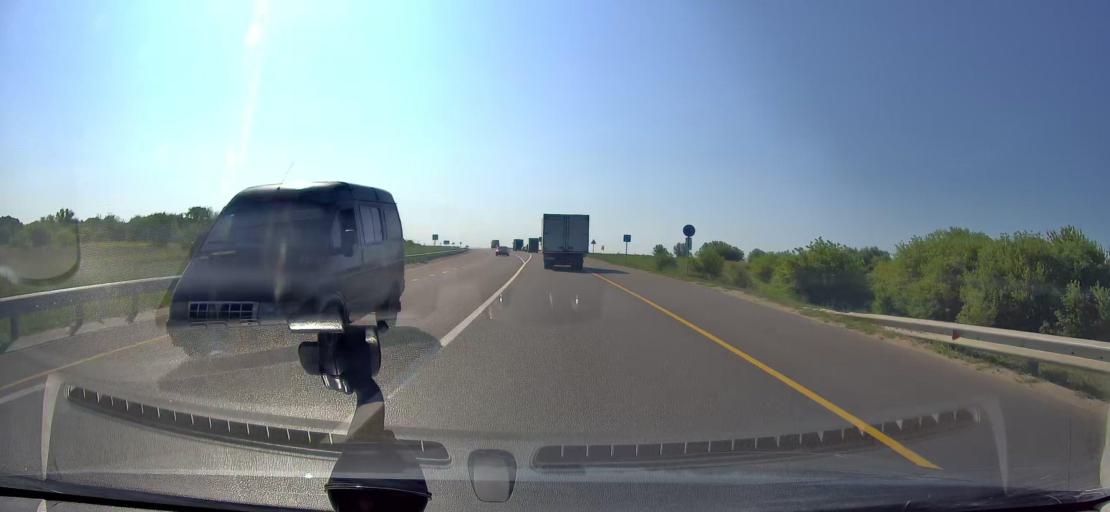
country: RU
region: Orjol
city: Kromy
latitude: 52.6566
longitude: 35.7173
